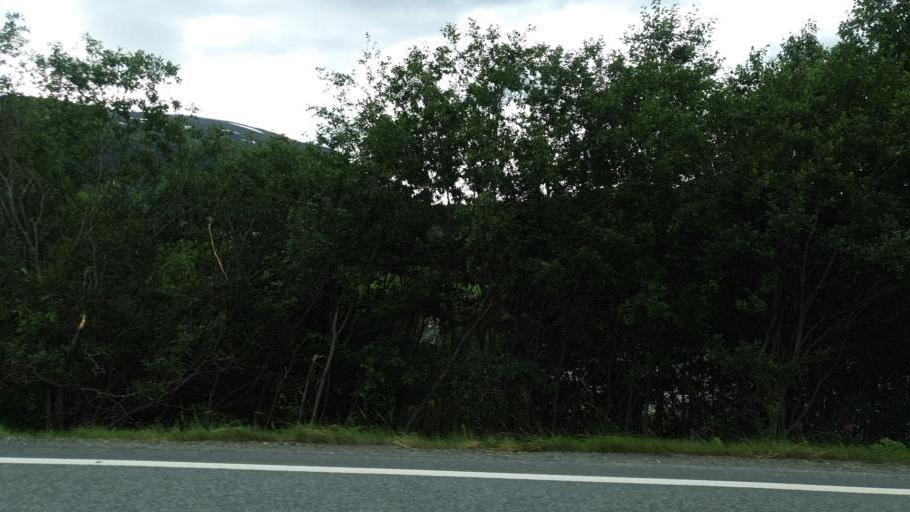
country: NO
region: Sor-Trondelag
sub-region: Oppdal
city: Oppdal
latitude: 62.5554
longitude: 9.6343
